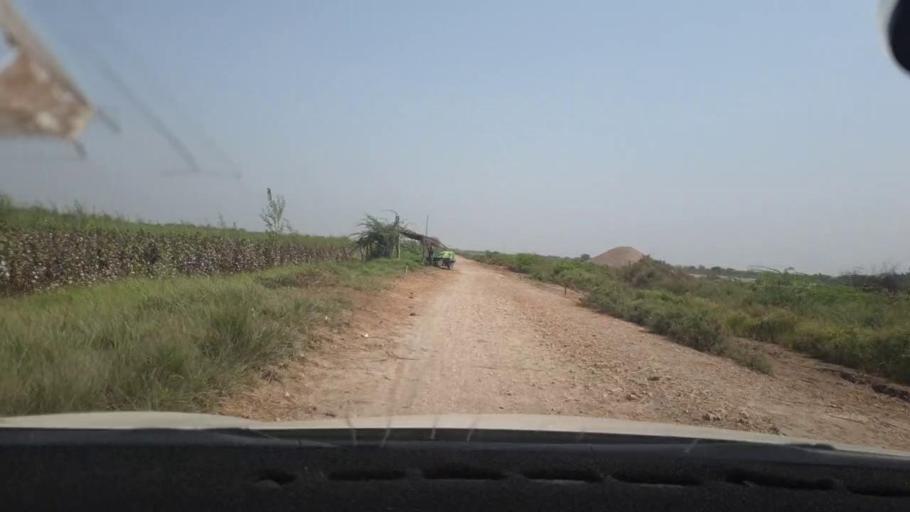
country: PK
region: Sindh
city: Tando Mittha Khan
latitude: 25.9231
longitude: 69.2271
